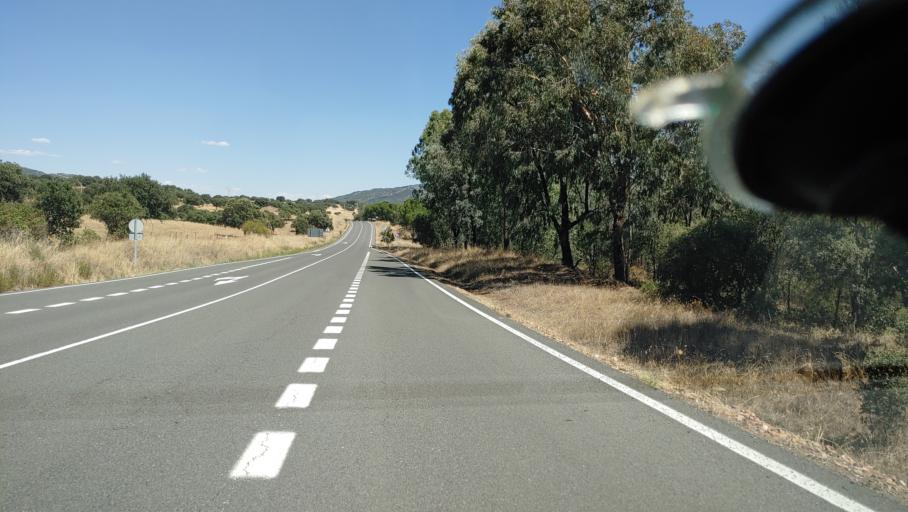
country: ES
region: Castille-La Mancha
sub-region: Provincia de Ciudad Real
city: Almaden
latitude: 38.8282
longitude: -4.7122
